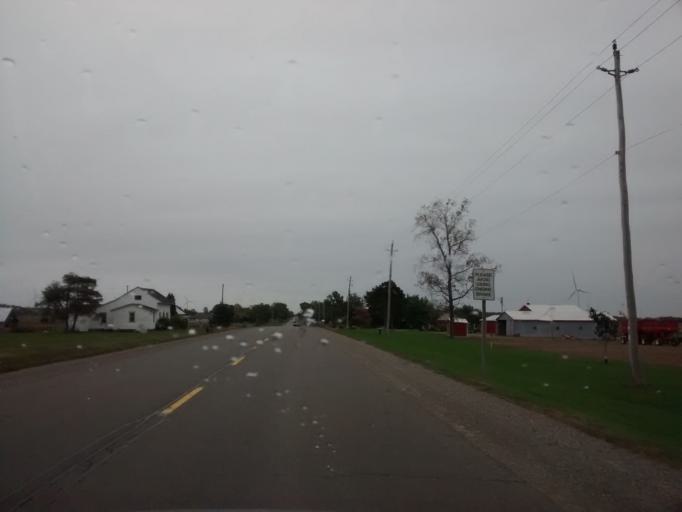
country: CA
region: Ontario
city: Ancaster
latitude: 42.8466
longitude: -79.8547
